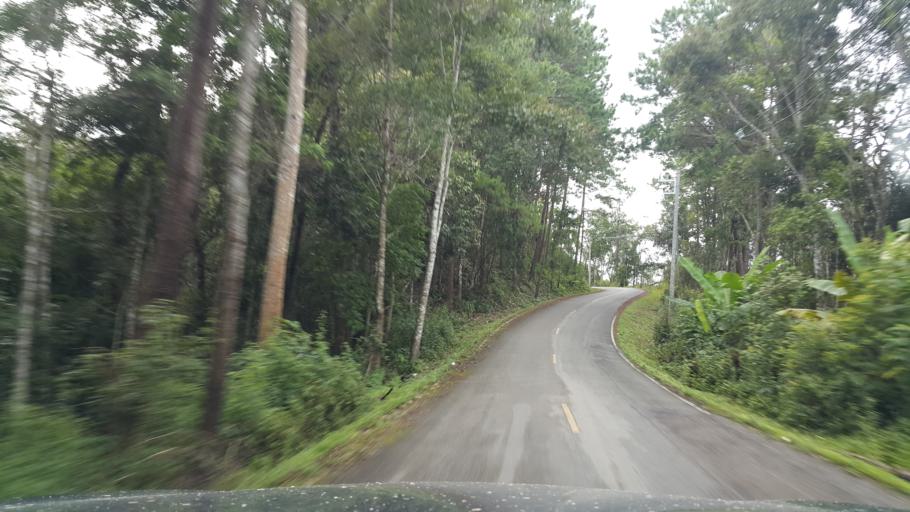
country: TH
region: Chiang Mai
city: Samoeng
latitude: 18.9129
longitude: 98.5001
